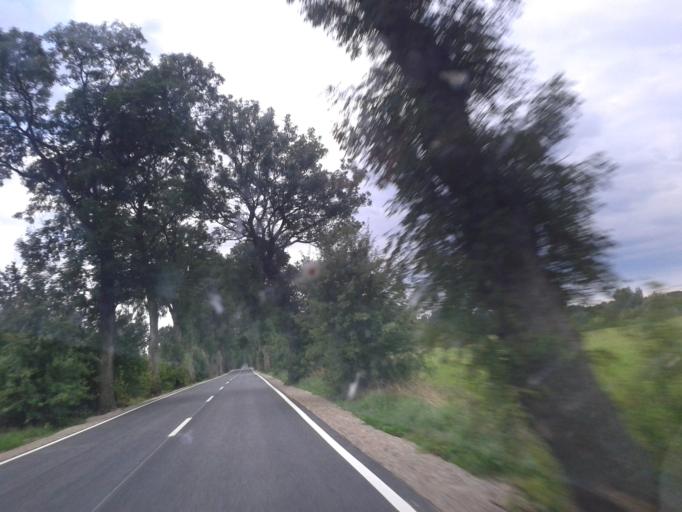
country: PL
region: West Pomeranian Voivodeship
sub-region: Powiat szczecinecki
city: Grzmiaca
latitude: 53.8634
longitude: 16.4799
